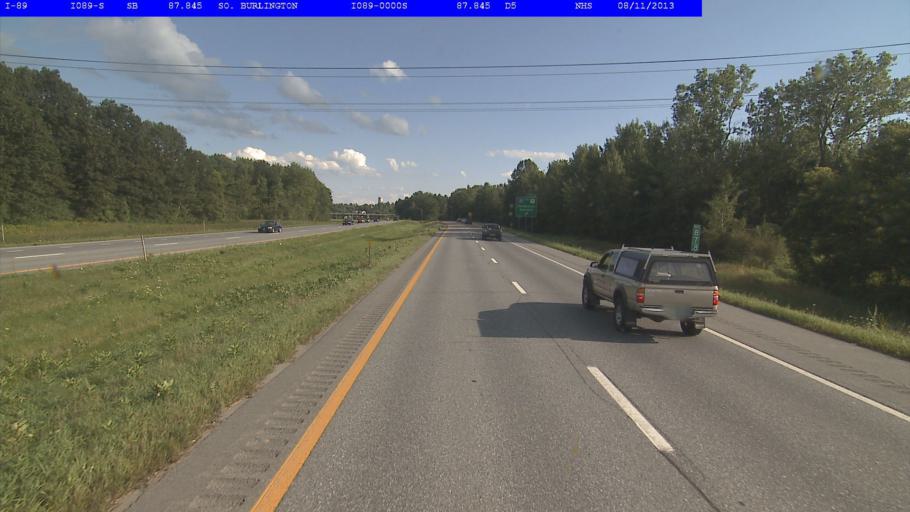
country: US
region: Vermont
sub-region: Chittenden County
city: South Burlington
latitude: 44.4574
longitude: -73.1847
